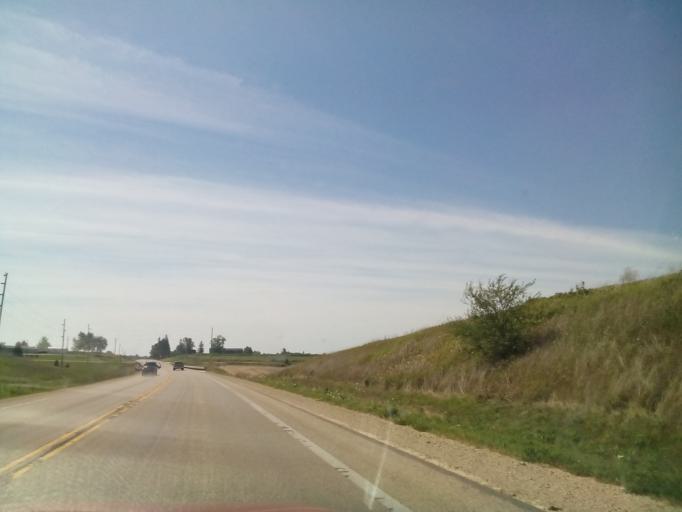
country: US
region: Wisconsin
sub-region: Green County
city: Monroe
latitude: 42.6498
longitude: -89.6315
